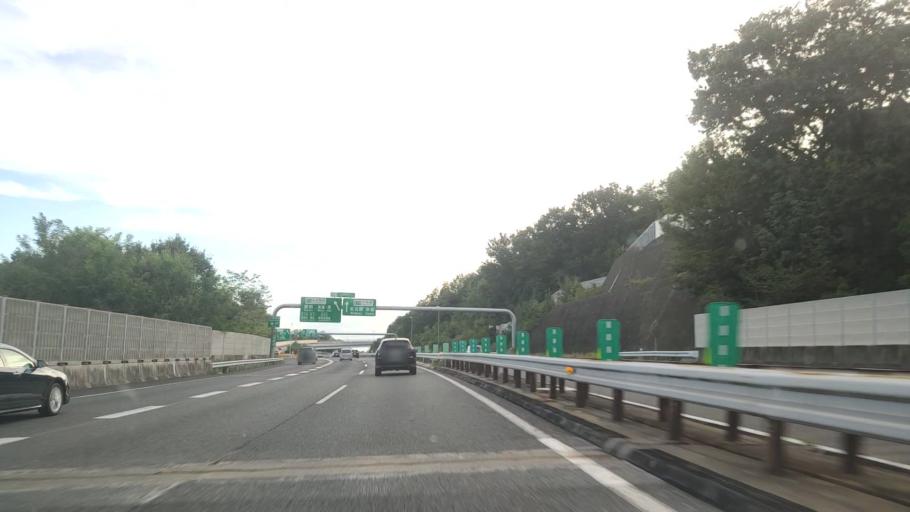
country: JP
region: Gifu
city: Toki
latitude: 35.3663
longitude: 137.1754
